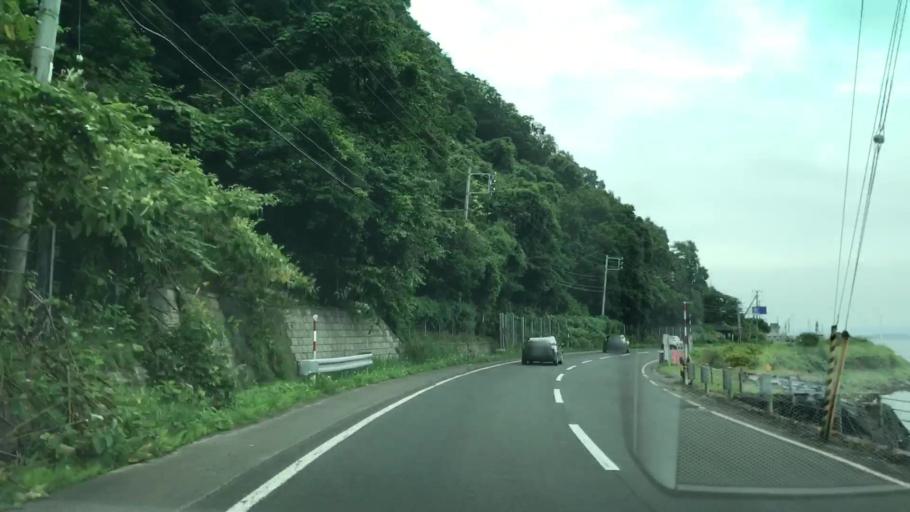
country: JP
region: Hokkaido
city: Iwanai
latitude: 42.7953
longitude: 140.3104
